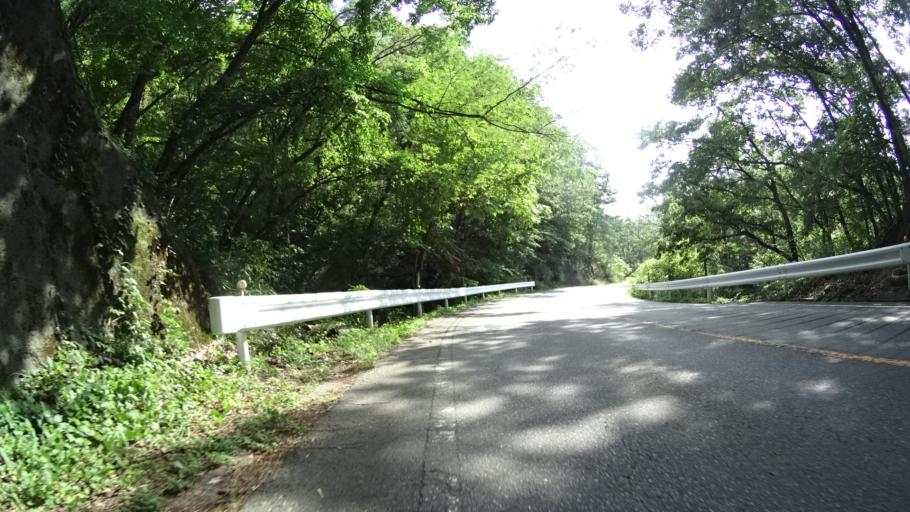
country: JP
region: Yamanashi
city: Kofu-shi
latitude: 35.7195
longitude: 138.5553
